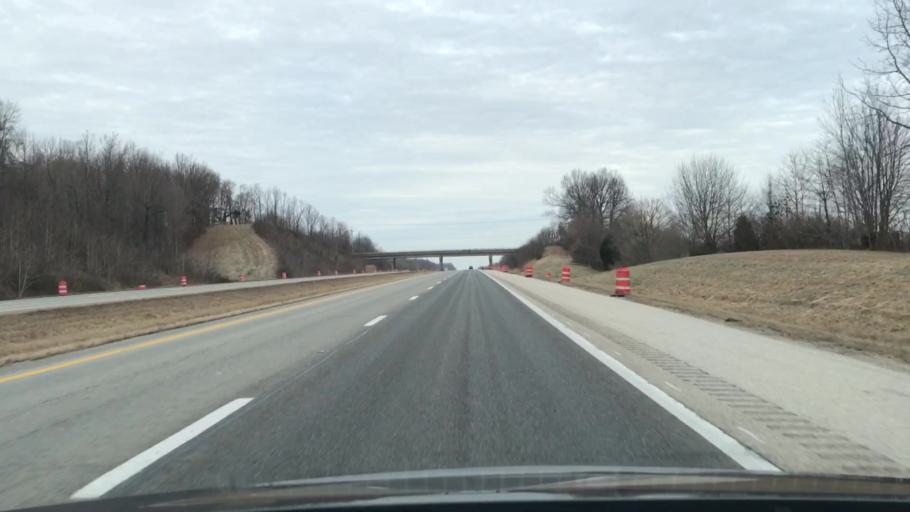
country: US
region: Kentucky
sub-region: Daviess County
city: Masonville
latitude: 37.6148
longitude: -86.9824
